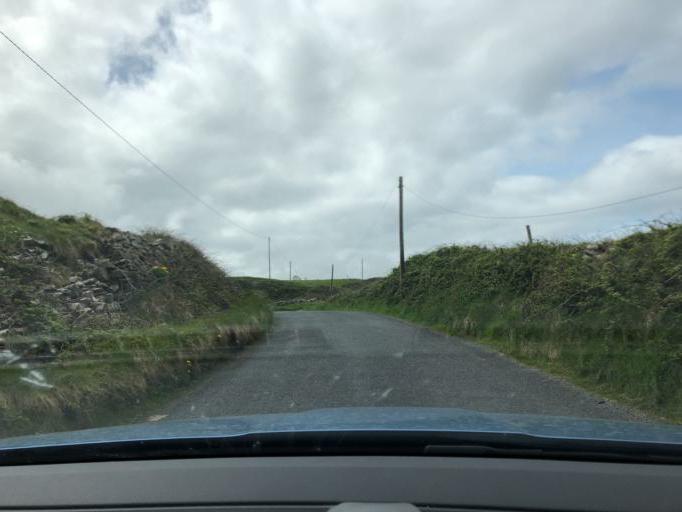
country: IE
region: Connaught
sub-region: County Galway
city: Bearna
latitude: 53.0115
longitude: -9.3862
